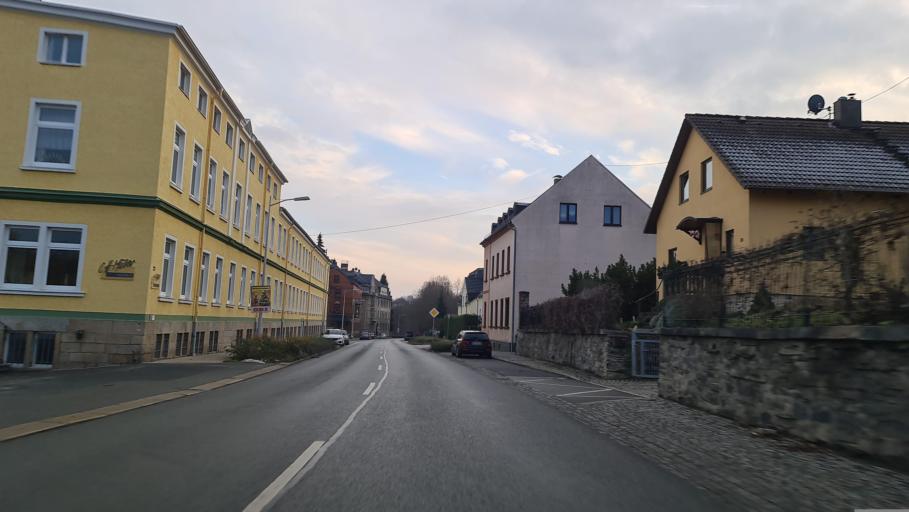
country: DE
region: Saxony
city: Netzschkau
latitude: 50.6112
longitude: 12.2488
